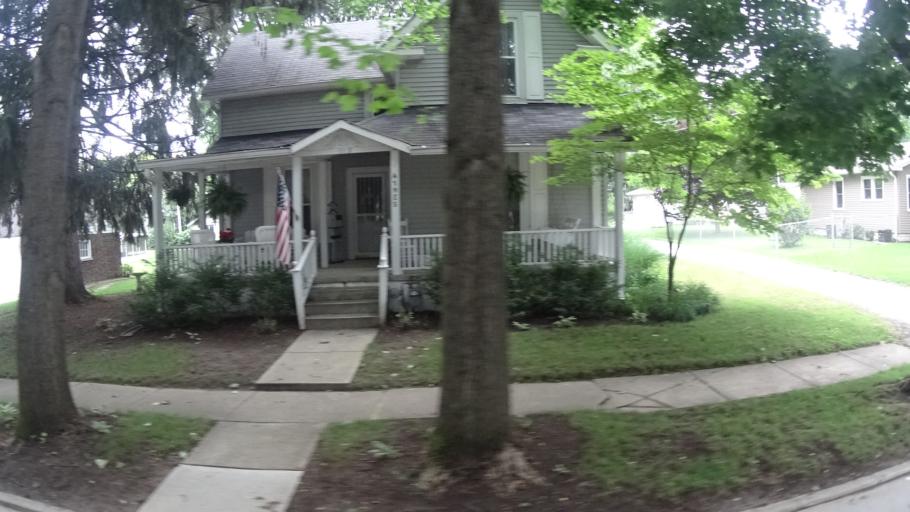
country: US
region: Indiana
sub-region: Madison County
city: Pendleton
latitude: 40.0019
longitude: -85.7518
